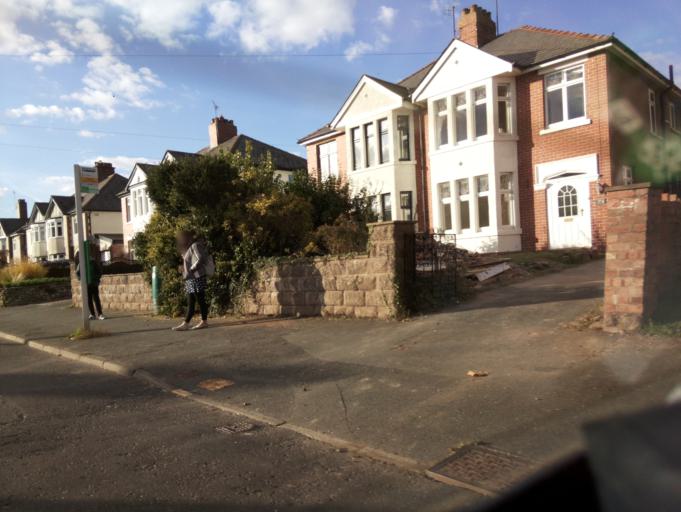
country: GB
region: England
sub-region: Herefordshire
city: Lower Bullingham
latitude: 52.0587
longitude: -2.6818
